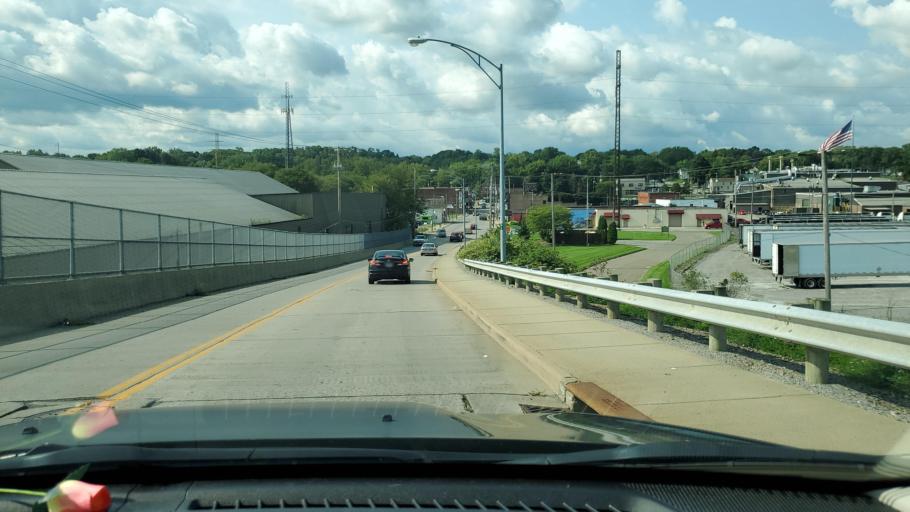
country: US
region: Ohio
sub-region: Mahoning County
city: Struthers
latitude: 41.0590
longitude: -80.5857
